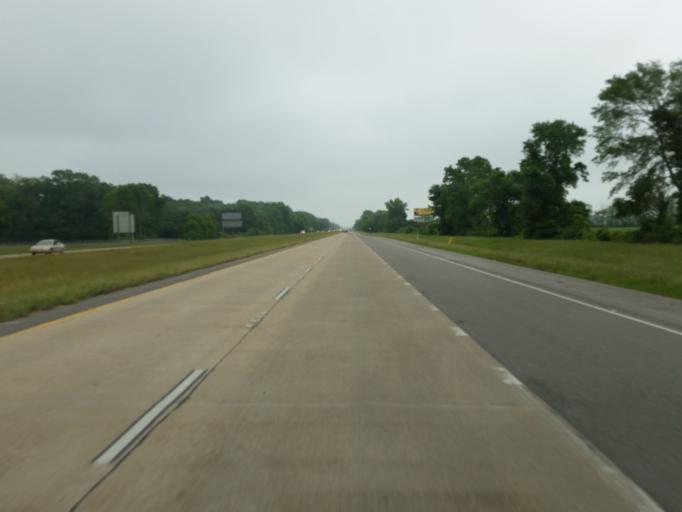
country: US
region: Louisiana
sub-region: Madison Parish
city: Tallulah
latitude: 32.3787
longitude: -91.1670
